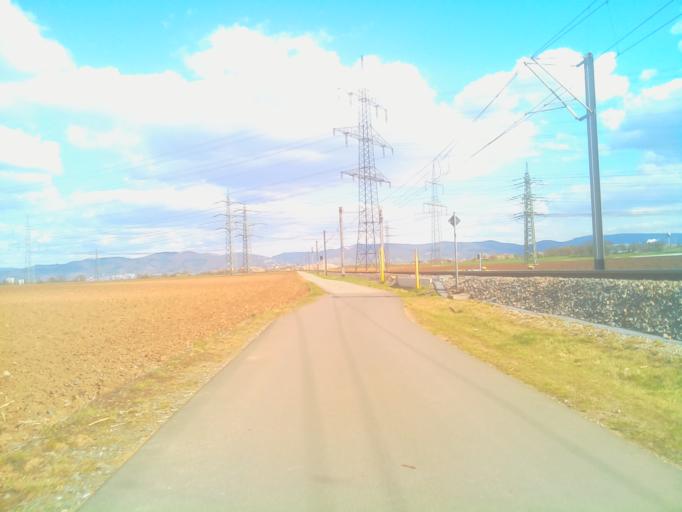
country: DE
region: Baden-Wuerttemberg
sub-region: Karlsruhe Region
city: Ilvesheim
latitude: 49.4959
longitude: 8.5608
